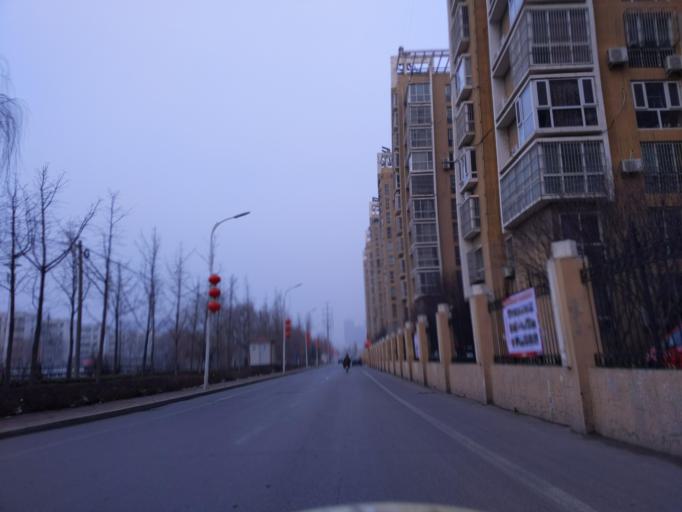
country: CN
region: Henan Sheng
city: Zhongyuanlu
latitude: 35.7659
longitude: 115.0477
